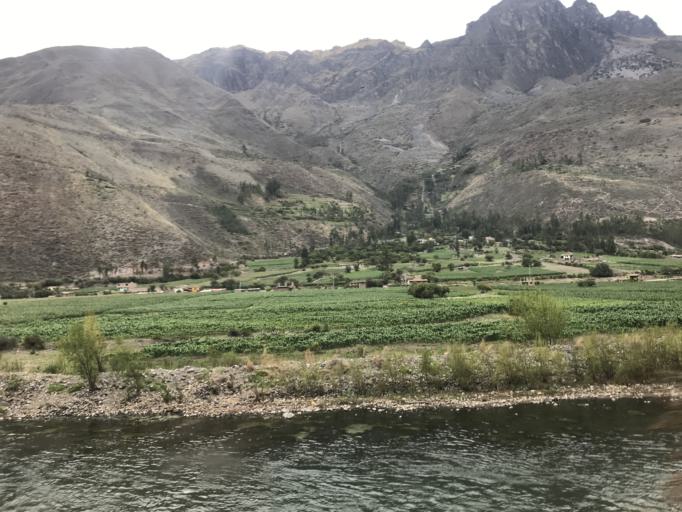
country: PE
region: Cusco
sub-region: Provincia de Urubamba
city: Ollantaytambo
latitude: -13.2512
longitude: -72.2846
